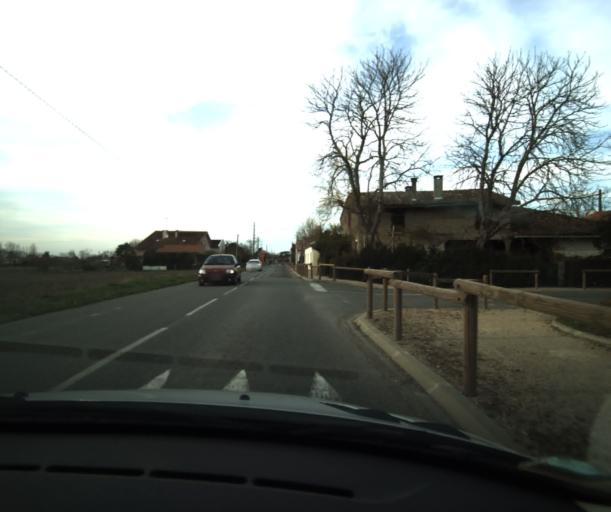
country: FR
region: Midi-Pyrenees
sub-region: Departement du Tarn-et-Garonne
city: Montech
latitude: 43.9514
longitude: 1.2324
